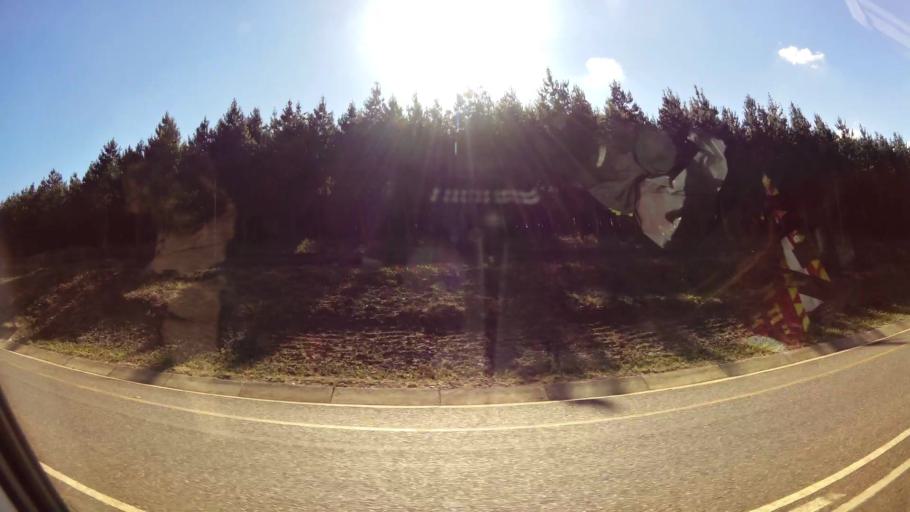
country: ZA
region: Limpopo
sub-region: Capricorn District Municipality
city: Mankoeng
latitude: -23.9116
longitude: 29.9664
